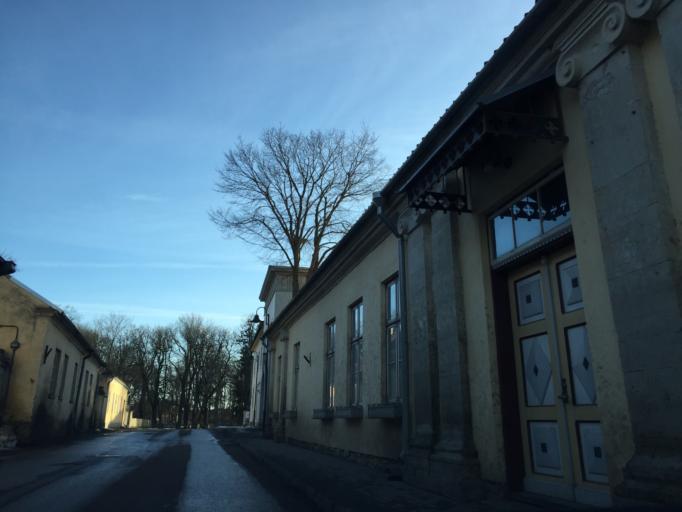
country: EE
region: Saare
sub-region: Kuressaare linn
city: Kuressaare
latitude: 58.2511
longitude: 22.4797
